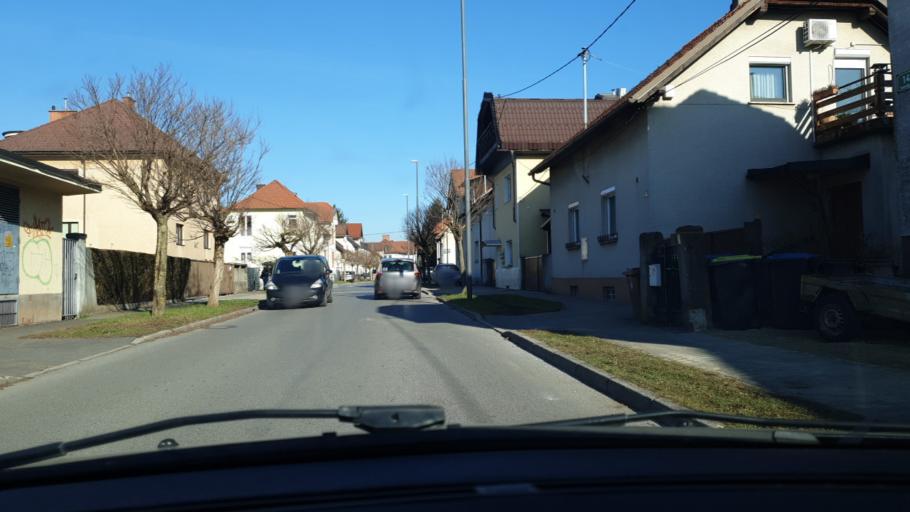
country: SI
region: Ljubljana
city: Ljubljana
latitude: 46.0595
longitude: 14.5288
